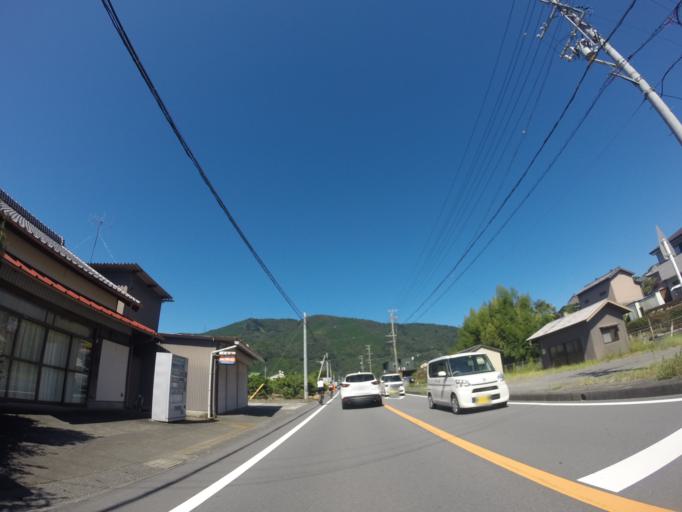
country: JP
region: Shizuoka
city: Kanaya
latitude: 34.8741
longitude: 138.1107
